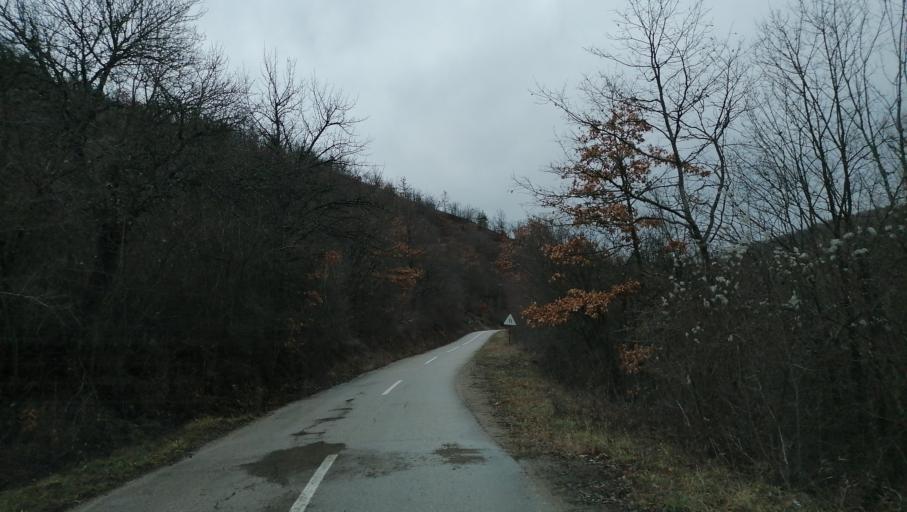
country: RS
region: Central Serbia
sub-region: Pirotski Okrug
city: Dimitrovgrad
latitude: 42.9523
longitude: 22.7773
